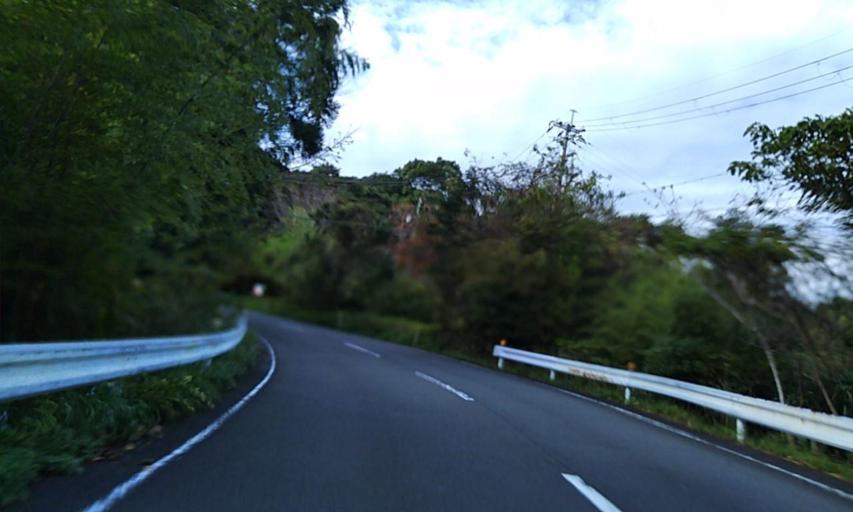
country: JP
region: Wakayama
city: Shingu
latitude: 33.4697
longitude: 135.8229
